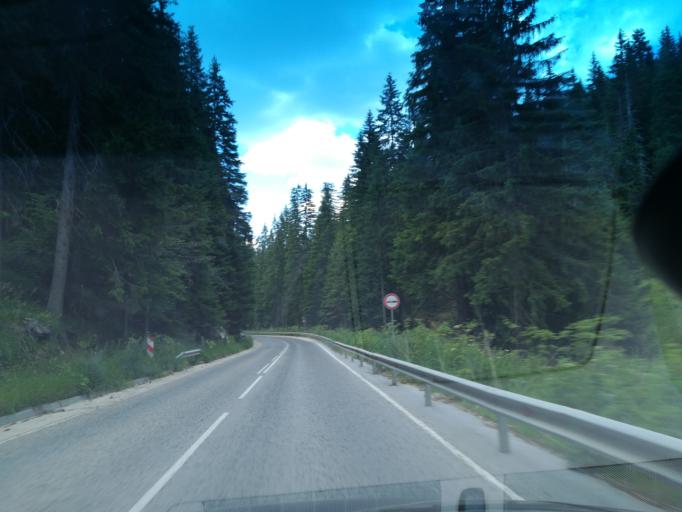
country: BG
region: Smolyan
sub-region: Obshtina Chepelare
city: Chepelare
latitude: 41.6608
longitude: 24.7134
